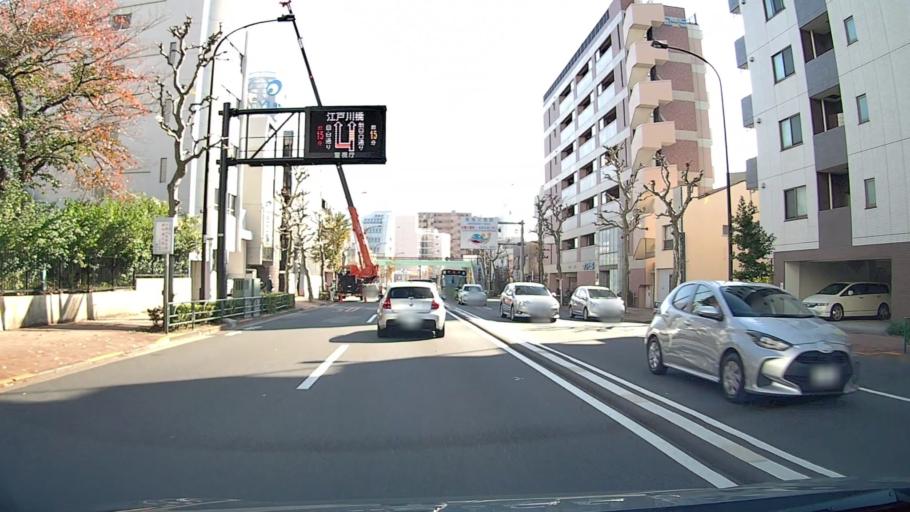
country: JP
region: Tokyo
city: Tokyo
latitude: 35.7285
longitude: 139.6795
